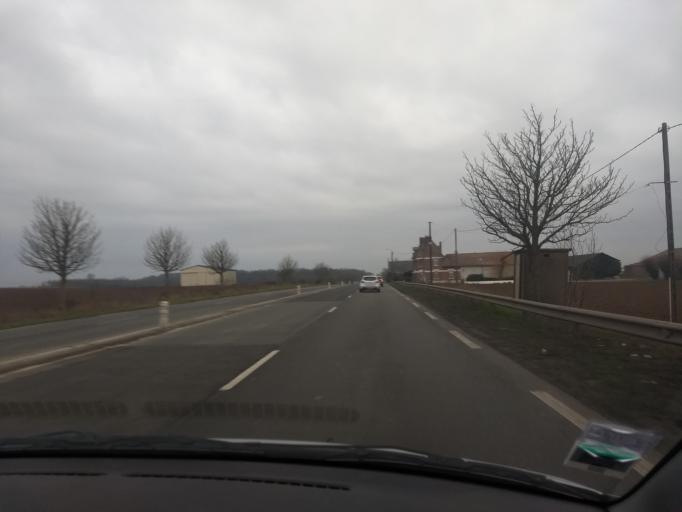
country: FR
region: Nord-Pas-de-Calais
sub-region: Departement du Pas-de-Calais
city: Feuchy
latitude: 50.2737
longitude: 2.8398
